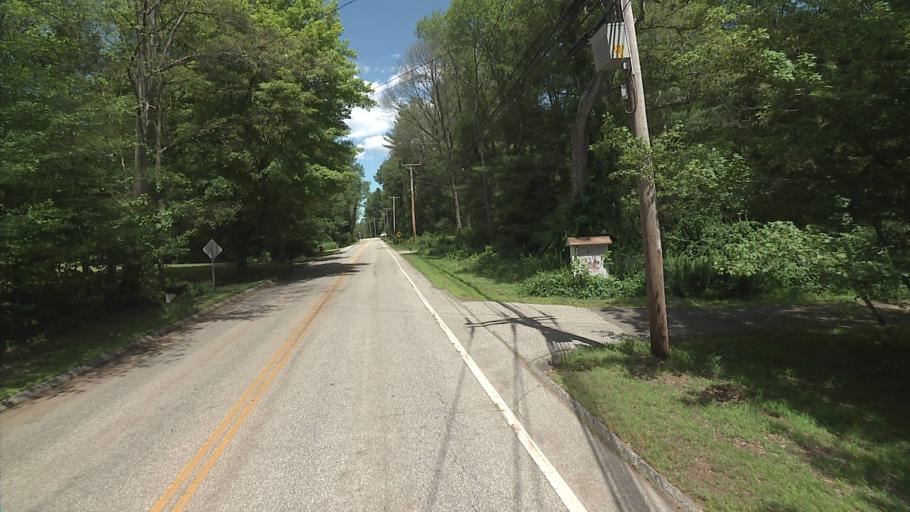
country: US
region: Connecticut
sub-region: Middlesex County
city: East Hampton
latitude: 41.5511
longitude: -72.5091
